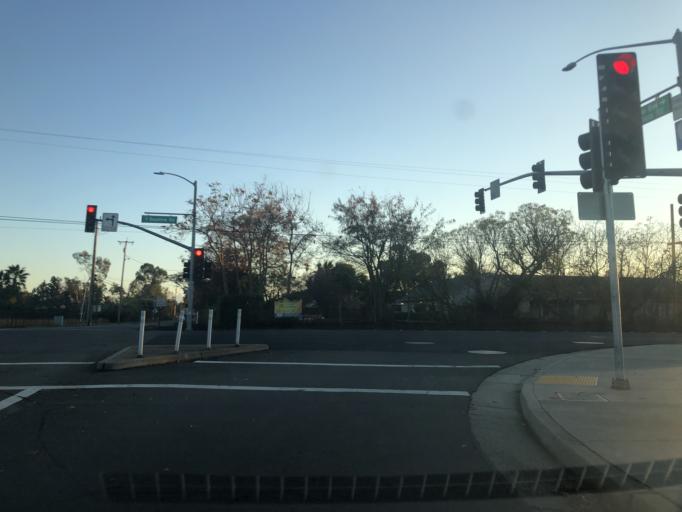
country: US
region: California
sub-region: Sacramento County
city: Antelope
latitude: 38.7522
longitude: -121.3371
